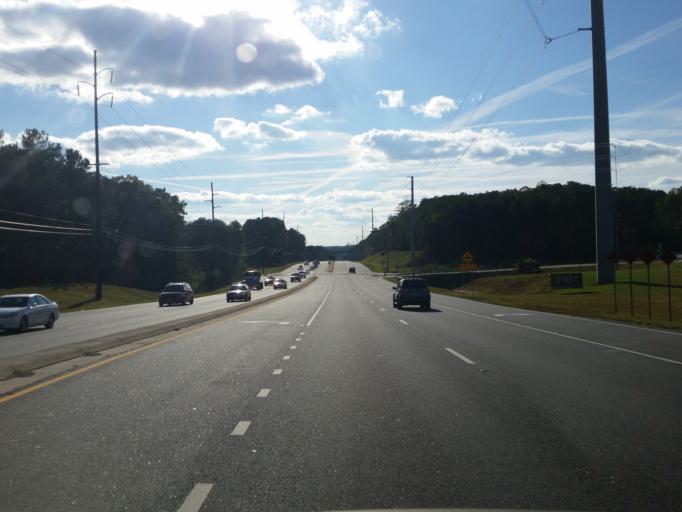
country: US
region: Georgia
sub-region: Paulding County
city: Hiram
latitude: 33.9388
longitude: -84.7097
